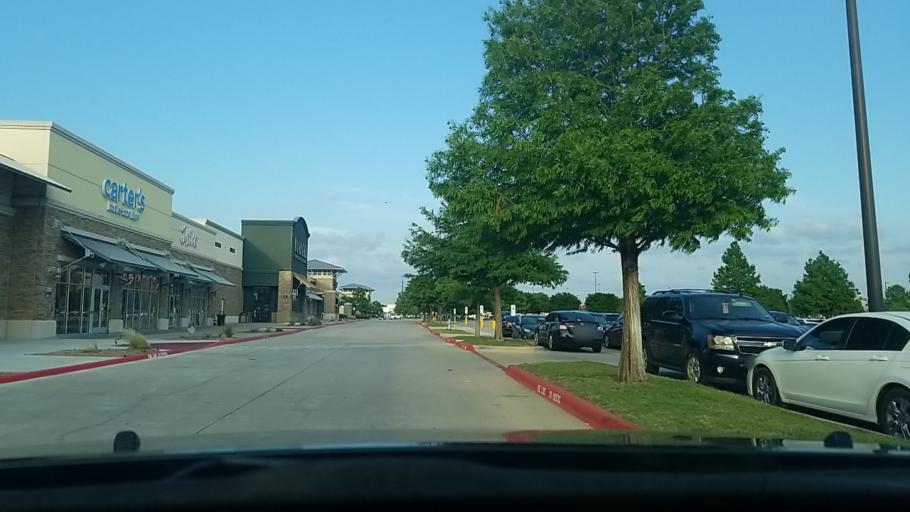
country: US
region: Texas
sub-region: Denton County
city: Denton
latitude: 33.1948
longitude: -97.0985
